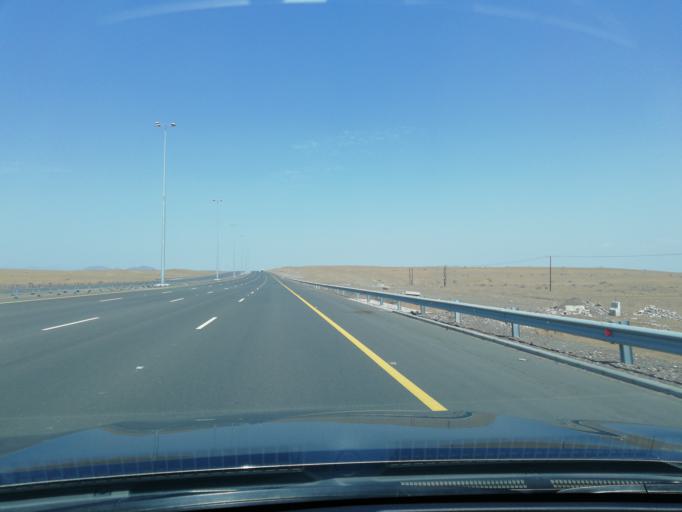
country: OM
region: Al Batinah
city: Rustaq
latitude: 23.5270
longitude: 57.6005
